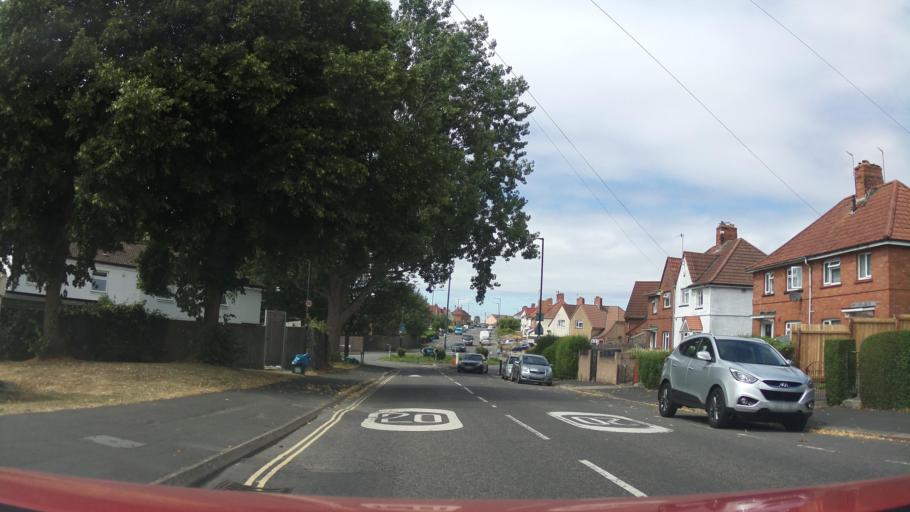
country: GB
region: England
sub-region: Bristol
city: Bristol
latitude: 51.4214
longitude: -2.5964
